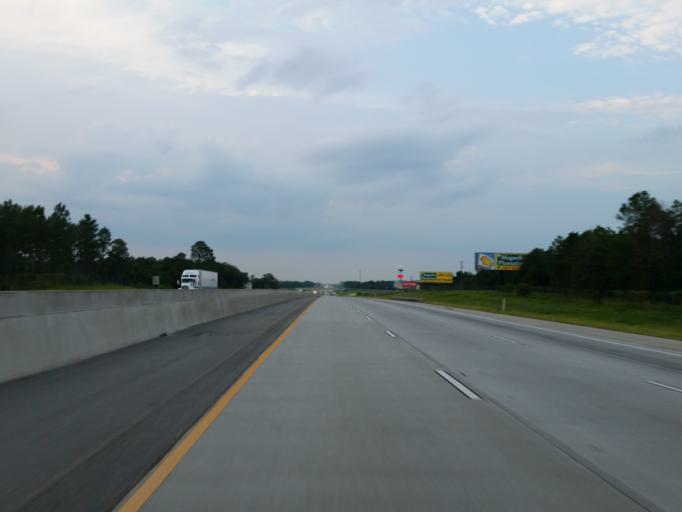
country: US
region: Georgia
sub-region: Tift County
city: Unionville
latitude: 31.3472
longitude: -83.4871
